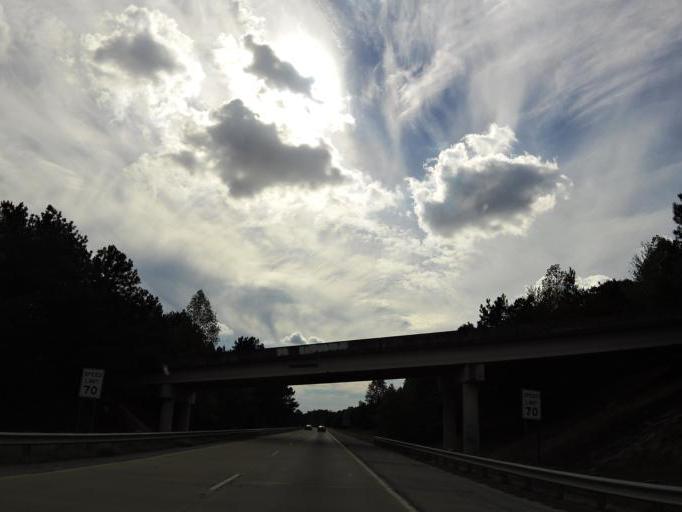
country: US
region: Georgia
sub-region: Cherokee County
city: Canton
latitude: 34.2764
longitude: -84.4592
